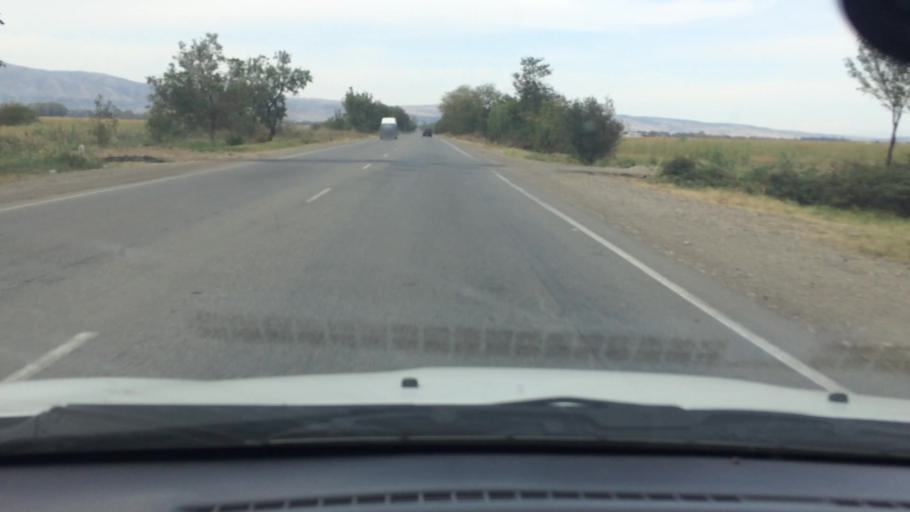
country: GE
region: Kvemo Kartli
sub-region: Marneuli
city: Marneuli
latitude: 41.5579
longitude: 44.7760
